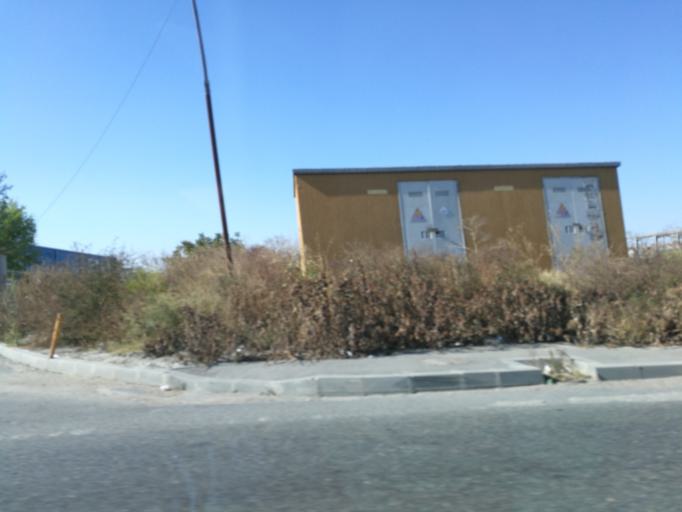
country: RO
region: Ilfov
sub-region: Comuna Chiajna
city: Chiajna
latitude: 44.4480
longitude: 25.9656
